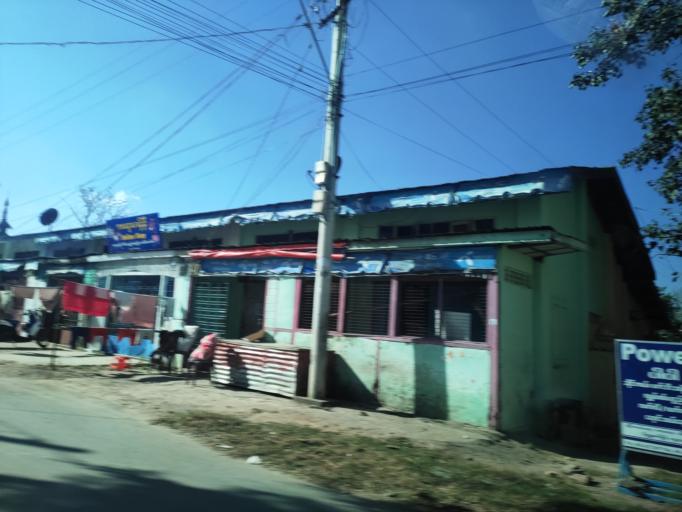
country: MM
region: Mandalay
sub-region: Pyin Oo Lwin District
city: Pyin Oo Lwin
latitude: 22.0354
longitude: 96.4817
